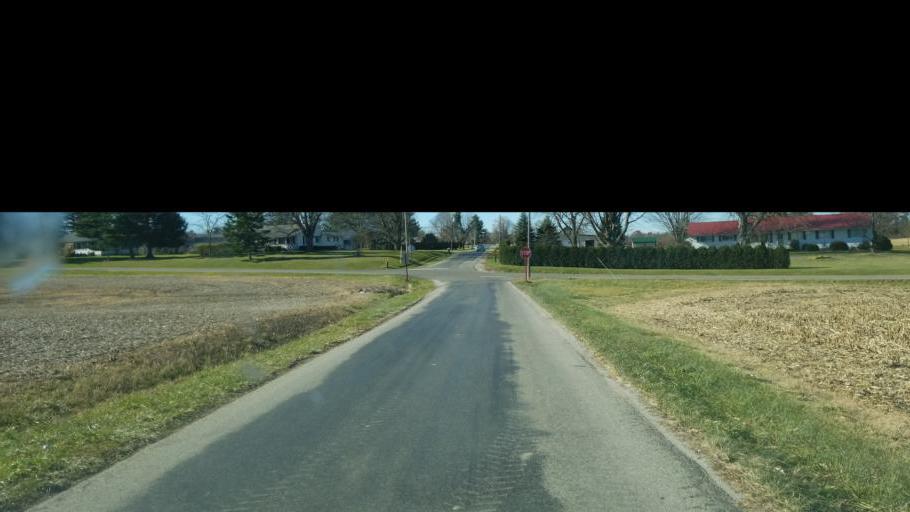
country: US
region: Ohio
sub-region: Huron County
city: Plymouth
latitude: 40.9703
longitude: -82.6754
